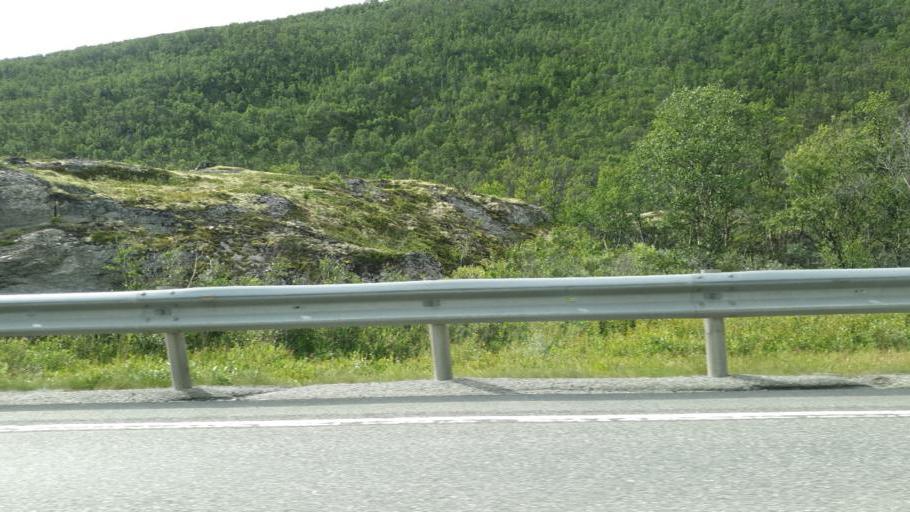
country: NO
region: Sor-Trondelag
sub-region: Oppdal
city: Oppdal
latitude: 62.3119
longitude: 9.6131
